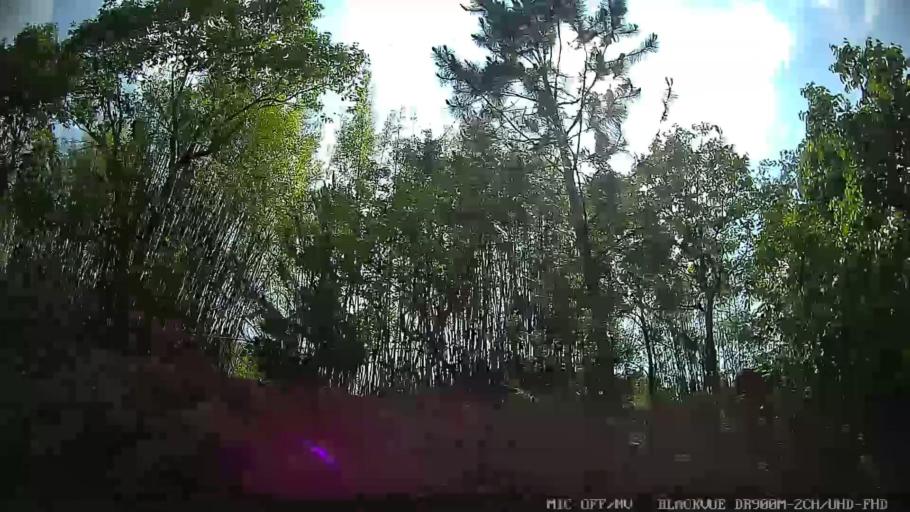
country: BR
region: Sao Paulo
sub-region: Braganca Paulista
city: Braganca Paulista
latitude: -22.9522
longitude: -46.5903
